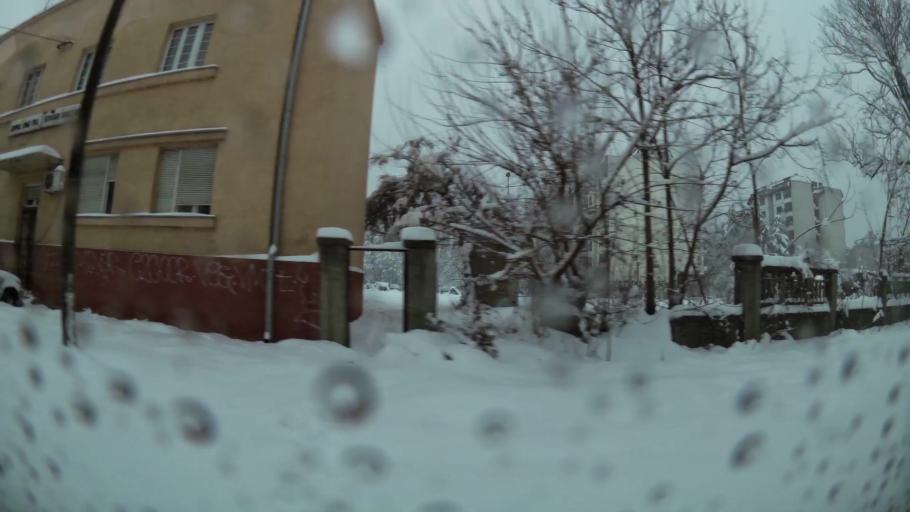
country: RS
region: Central Serbia
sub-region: Belgrade
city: Stari Grad
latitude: 44.8286
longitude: 20.4583
